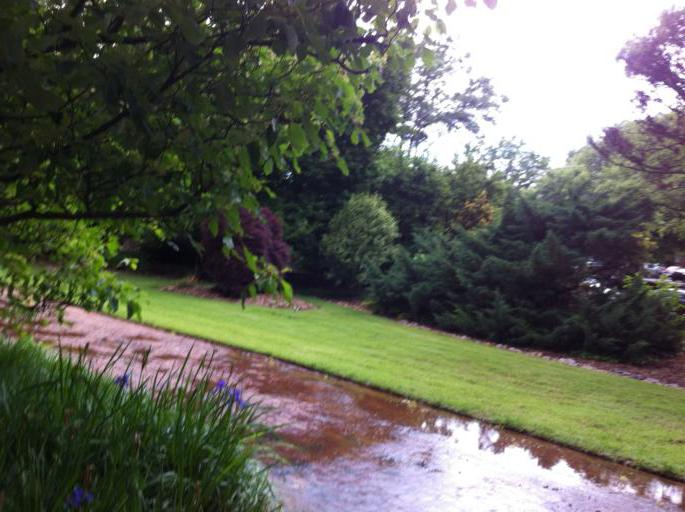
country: US
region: North Carolina
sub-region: Wake County
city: West Raleigh
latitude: 35.7885
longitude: -78.6726
